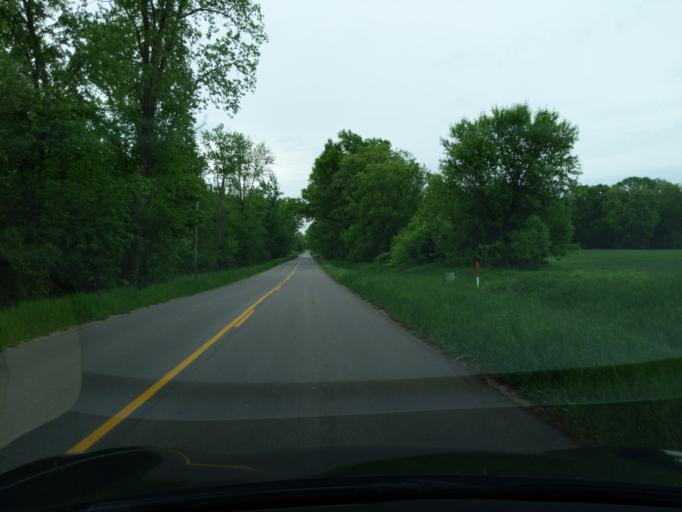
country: US
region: Michigan
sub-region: Jackson County
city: Jackson
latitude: 42.3454
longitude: -84.3486
